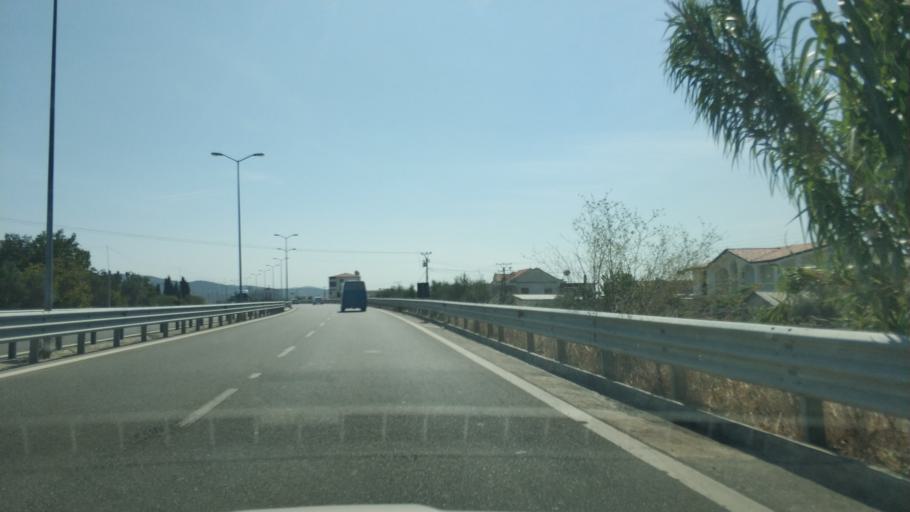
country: AL
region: Tirane
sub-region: Rrethi i Kavajes
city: Gose e Madhe
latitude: 41.0777
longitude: 19.6256
